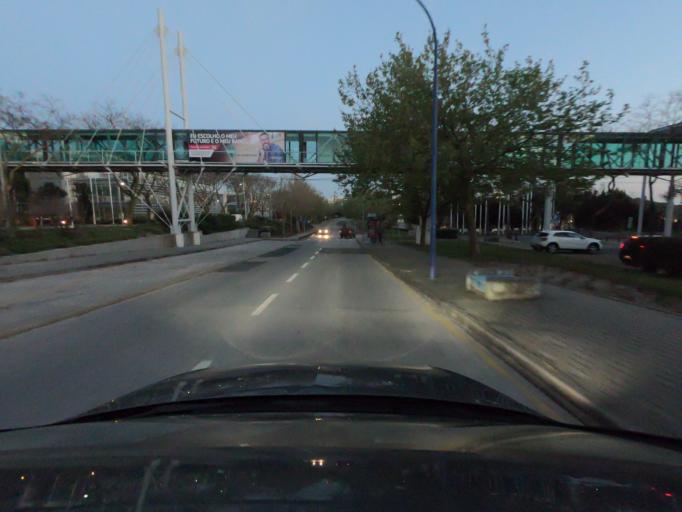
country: PT
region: Lisbon
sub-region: Sintra
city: Cacem
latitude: 38.7449
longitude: -9.3044
